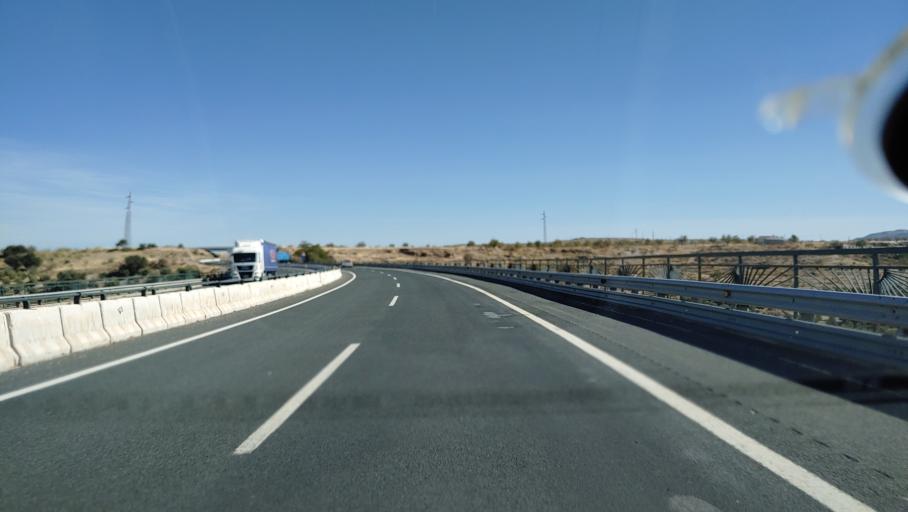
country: ES
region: Andalusia
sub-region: Provincia de Granada
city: Gor
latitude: 37.3931
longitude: -2.9962
